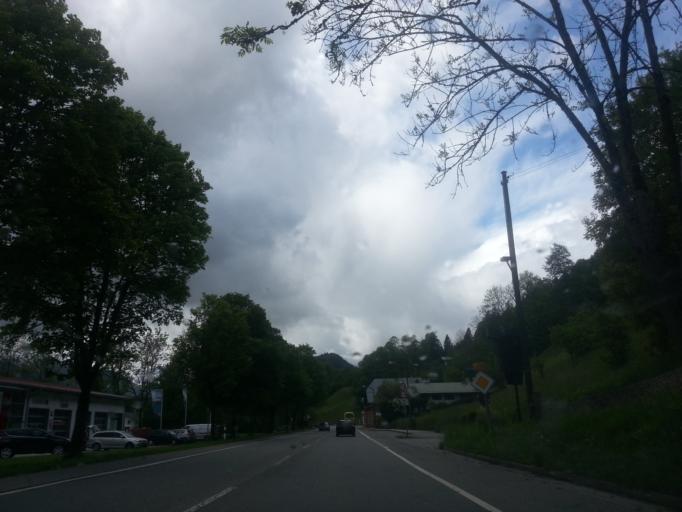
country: DE
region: Bavaria
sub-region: Upper Bavaria
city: Berchtesgaden
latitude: 47.6426
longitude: 13.0208
